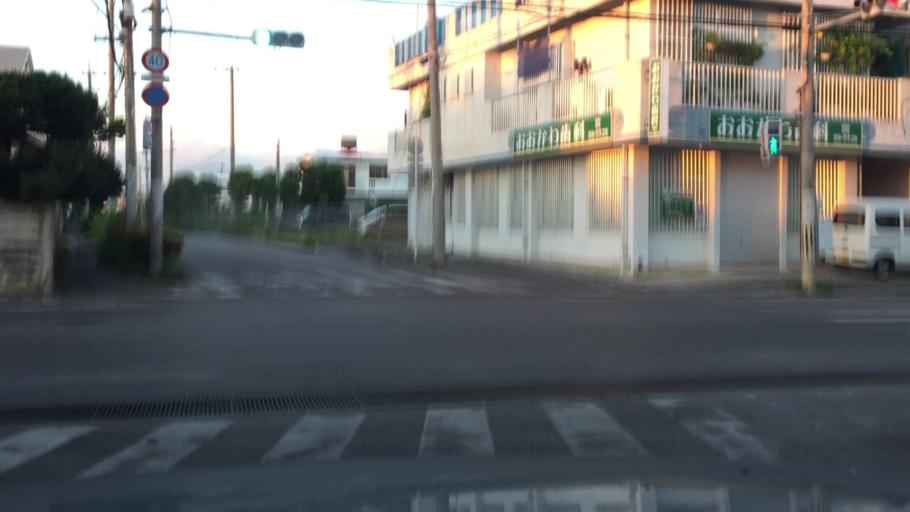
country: JP
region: Okinawa
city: Ishigaki
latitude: 24.3462
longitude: 124.1616
